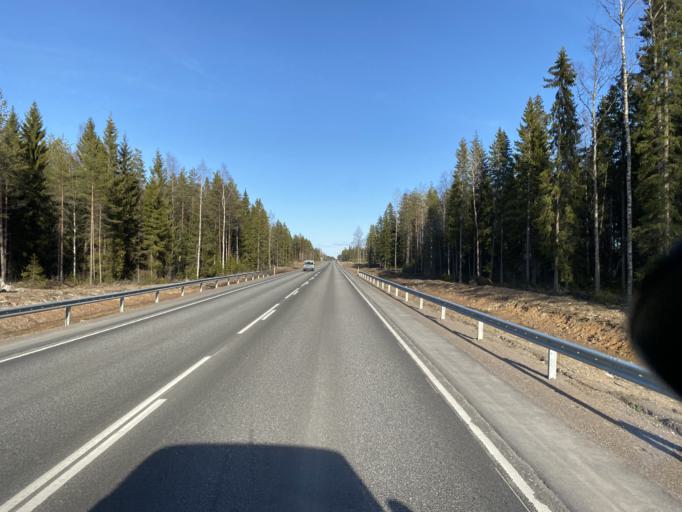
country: FI
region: Satakunta
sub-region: Pori
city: Kokemaeki
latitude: 61.1673
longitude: 22.4380
